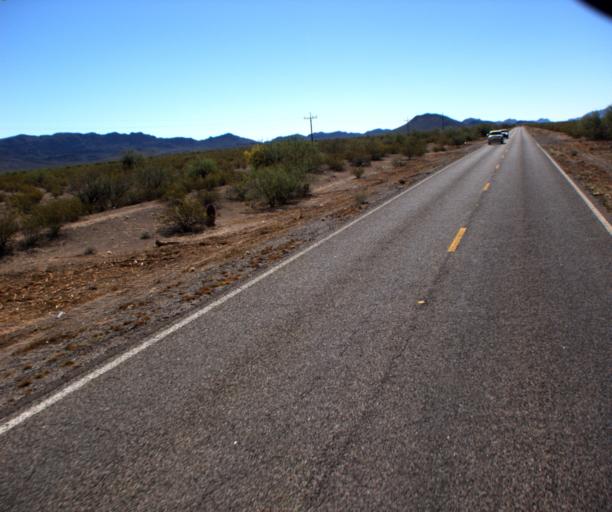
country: US
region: Arizona
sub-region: Pima County
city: Ajo
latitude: 32.3181
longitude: -112.7684
